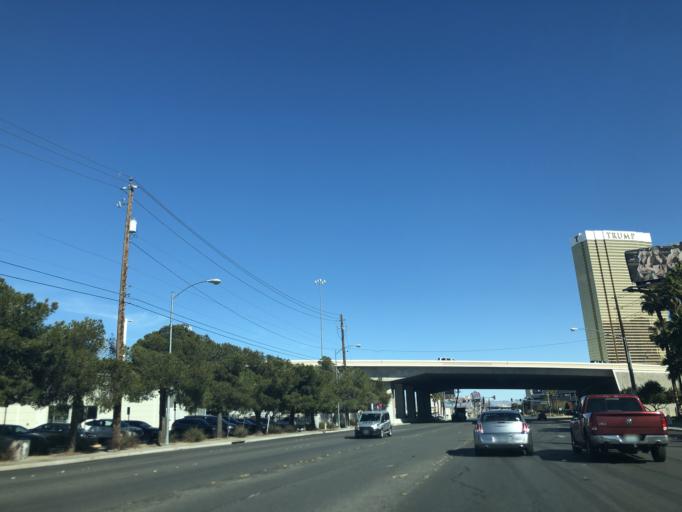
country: US
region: Nevada
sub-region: Clark County
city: Paradise
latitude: 36.1248
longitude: -115.1775
